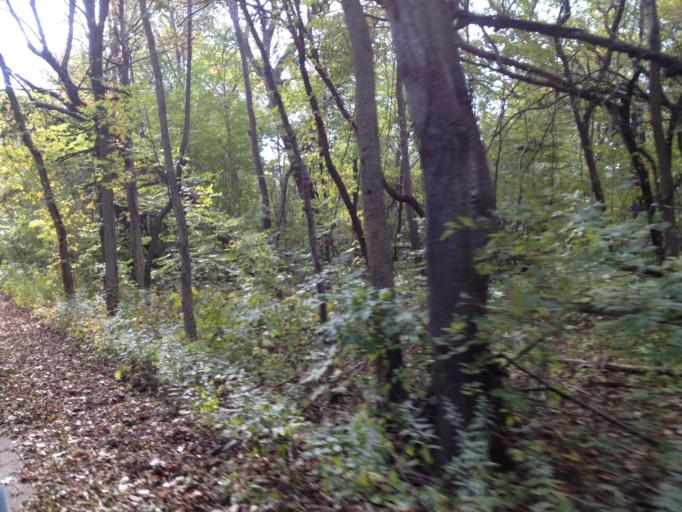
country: US
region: Ohio
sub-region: Erie County
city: Sandusky
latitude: 41.9299
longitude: -82.5138
